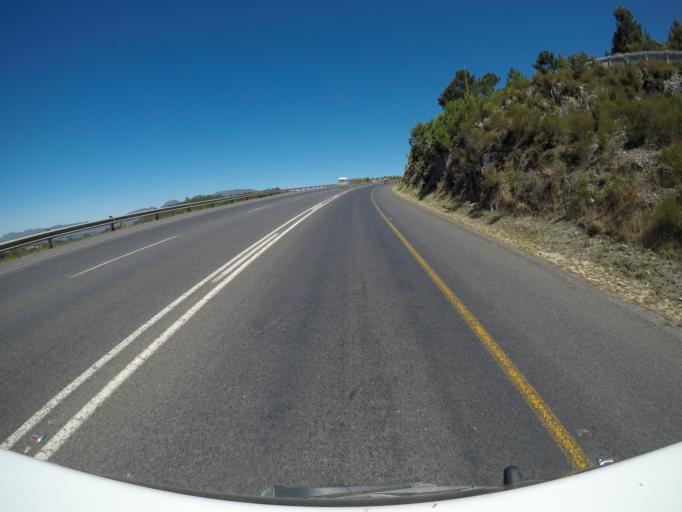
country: ZA
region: Western Cape
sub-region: Overberg District Municipality
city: Grabouw
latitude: -34.1667
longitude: 19.0004
